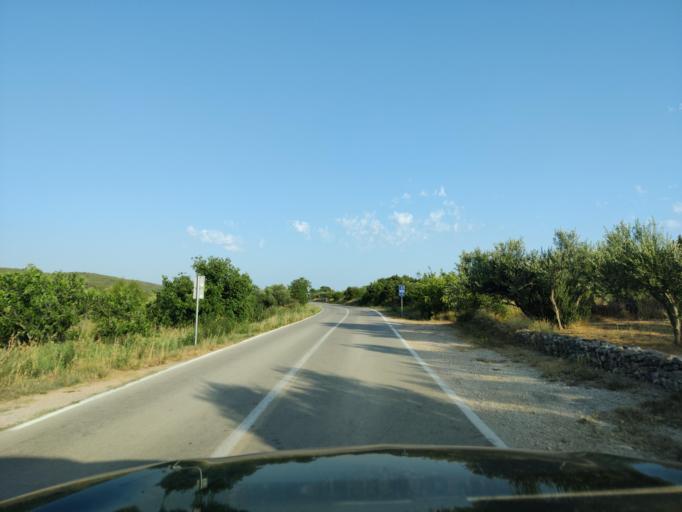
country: HR
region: Sibensko-Kniniska
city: Tribunj
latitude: 43.7821
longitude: 15.7129
